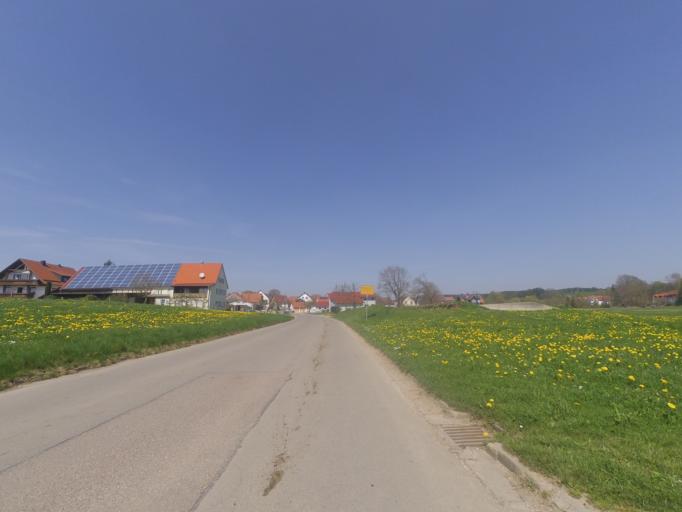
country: DE
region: Bavaria
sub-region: Swabia
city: Roggenburg
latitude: 48.2836
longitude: 10.2140
